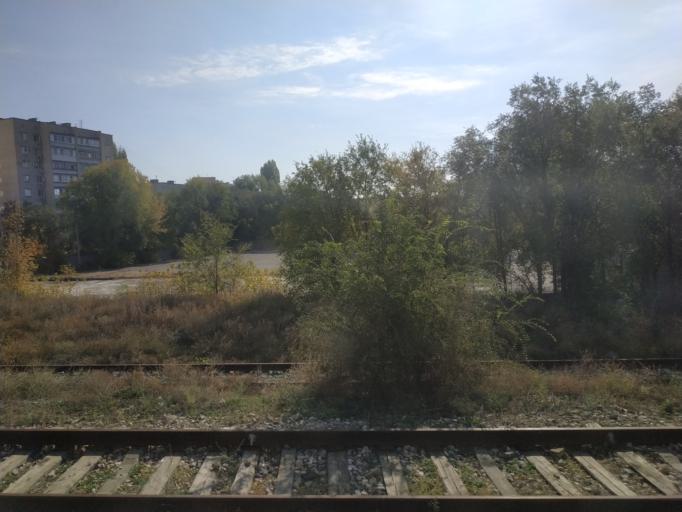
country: RU
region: Volgograd
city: Volgograd
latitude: 48.7306
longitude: 44.5313
